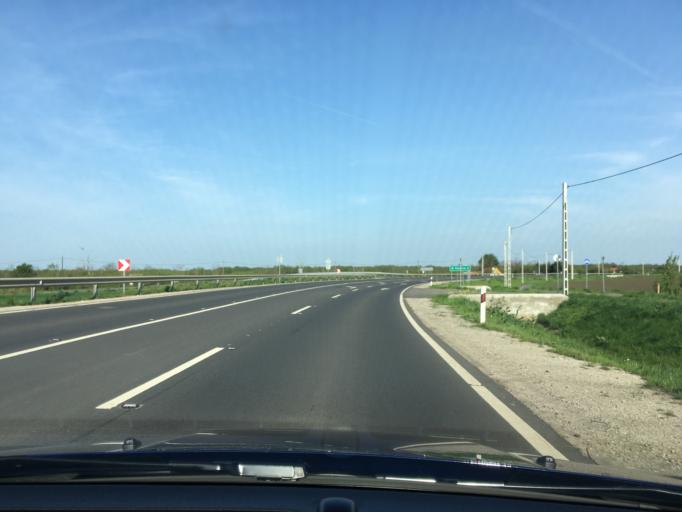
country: HU
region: Bekes
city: Csorvas
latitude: 46.6464
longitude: 20.8698
